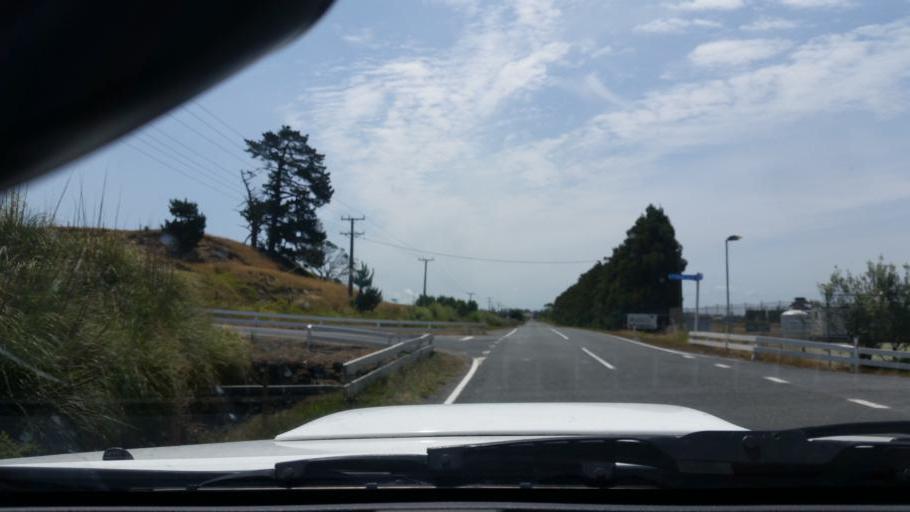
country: NZ
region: Northland
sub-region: Kaipara District
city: Dargaville
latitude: -36.0599
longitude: 173.9355
